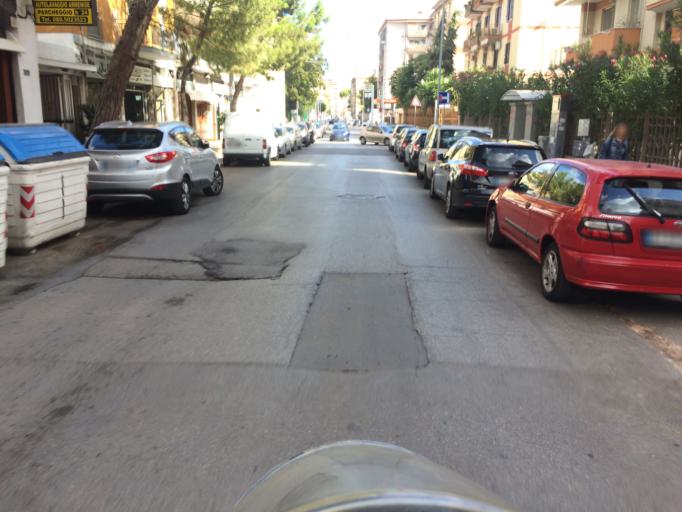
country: IT
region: Apulia
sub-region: Provincia di Bari
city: Bari
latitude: 41.1028
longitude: 16.8716
